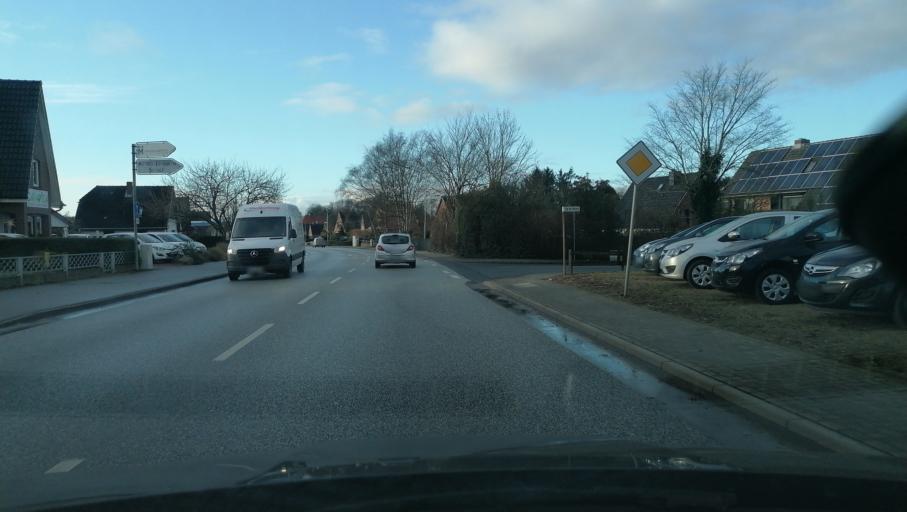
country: DE
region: Schleswig-Holstein
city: Nindorf
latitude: 54.0884
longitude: 9.0987
